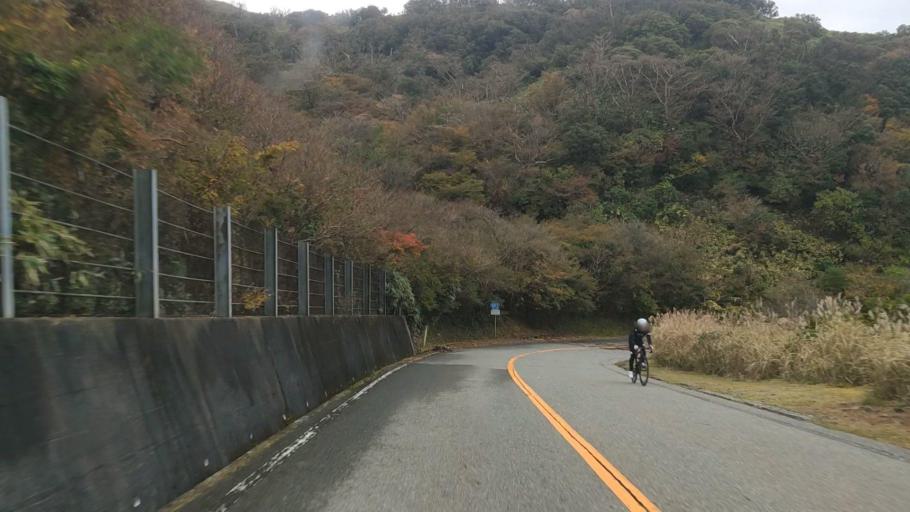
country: JP
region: Shizuoka
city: Heda
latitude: 34.9570
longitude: 138.8409
